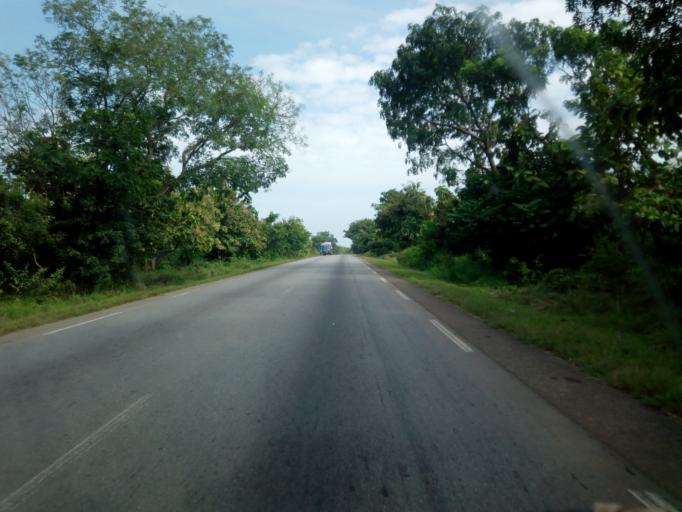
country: TG
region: Plateaux
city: Notse
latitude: 7.0510
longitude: 1.1548
